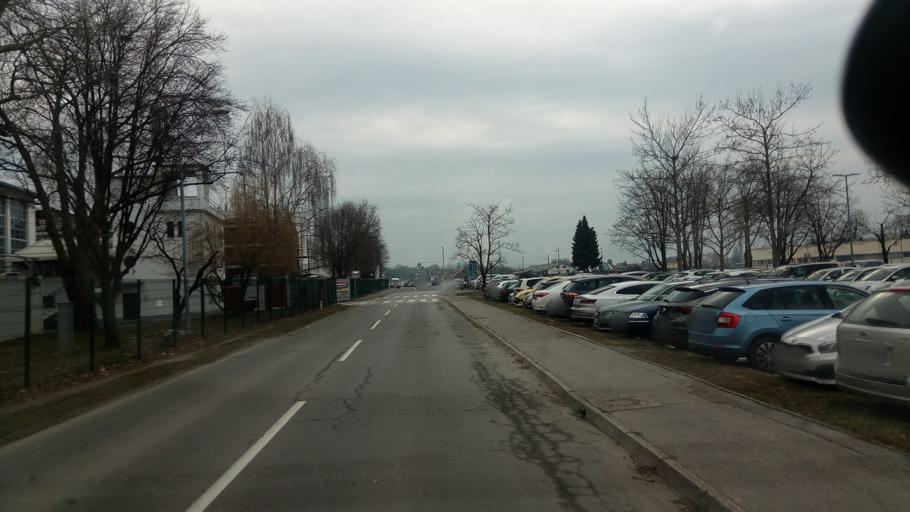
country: SI
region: Menges
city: Preserje pri Radomljah
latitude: 46.1682
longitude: 14.5865
